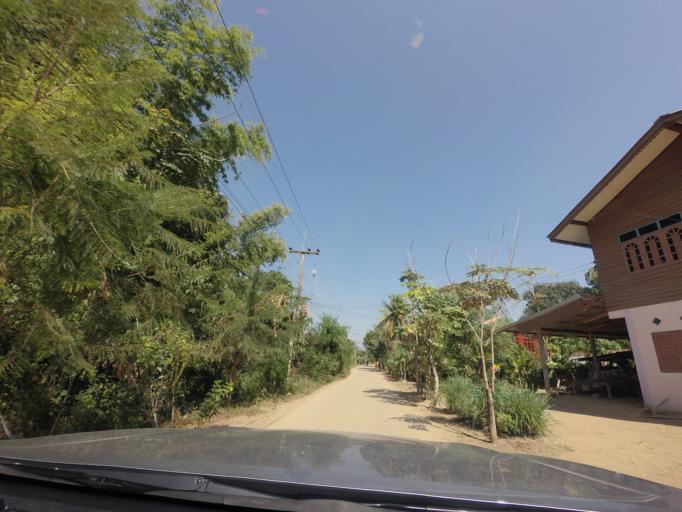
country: TH
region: Sukhothai
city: Si Samrong
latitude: 17.2001
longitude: 99.7728
